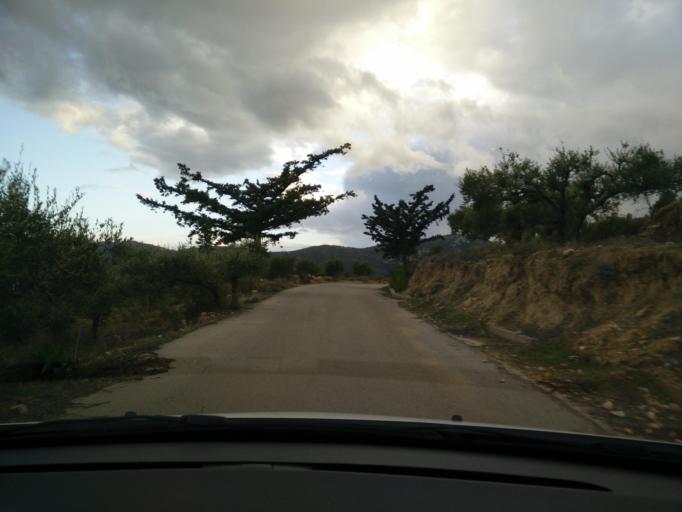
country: GR
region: Crete
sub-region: Nomos Lasithiou
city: Kritsa
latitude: 35.1056
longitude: 25.6951
